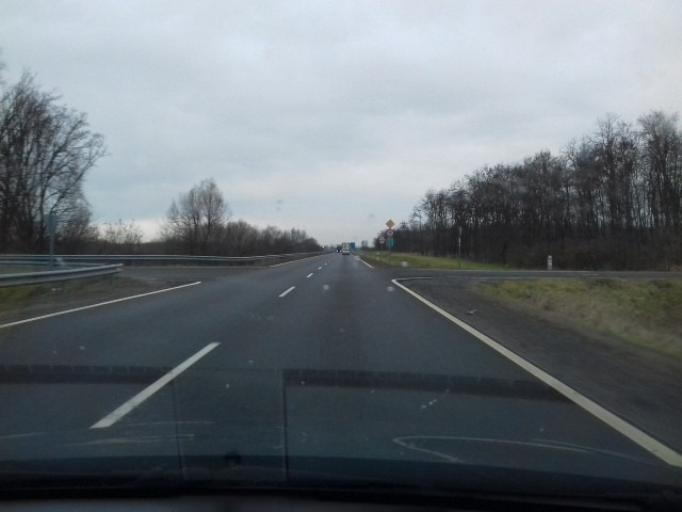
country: HU
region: Szabolcs-Szatmar-Bereg
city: Nagykallo
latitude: 47.9084
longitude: 21.8181
